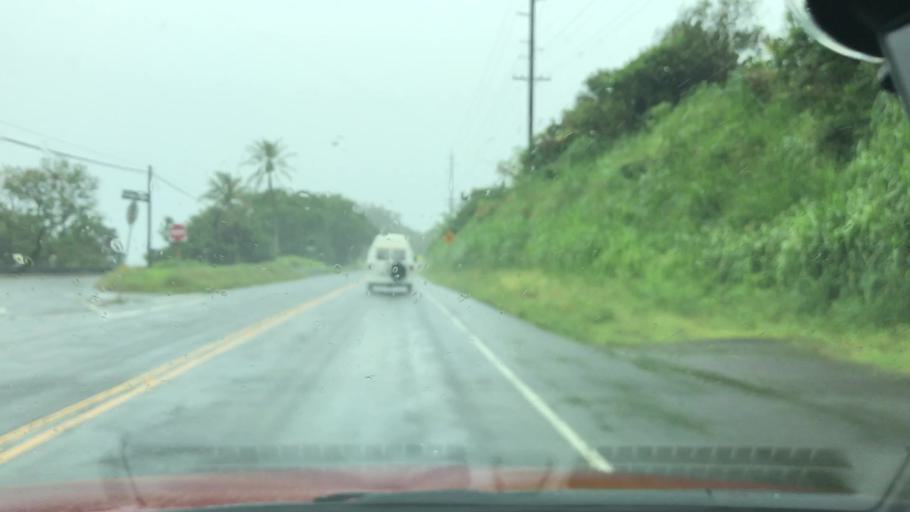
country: US
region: Hawaii
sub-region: Hawaii County
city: Pepeekeo
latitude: 19.9852
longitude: -155.2366
